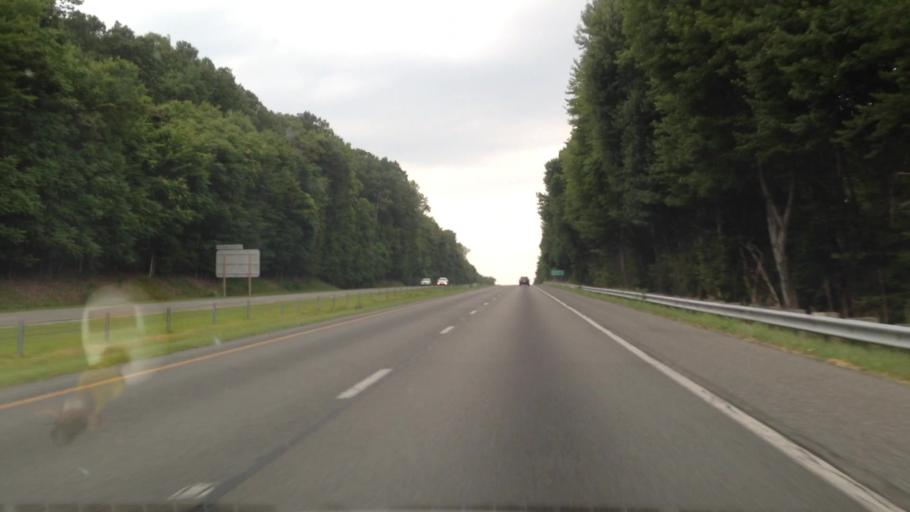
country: US
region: North Carolina
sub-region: Surry County
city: Pilot Mountain
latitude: 36.3456
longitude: -80.4626
